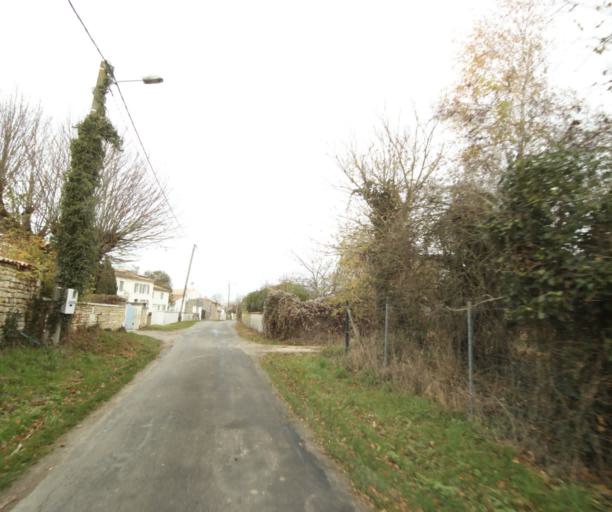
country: FR
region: Poitou-Charentes
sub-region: Departement de la Charente-Maritime
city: Corme-Royal
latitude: 45.7341
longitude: -0.7862
